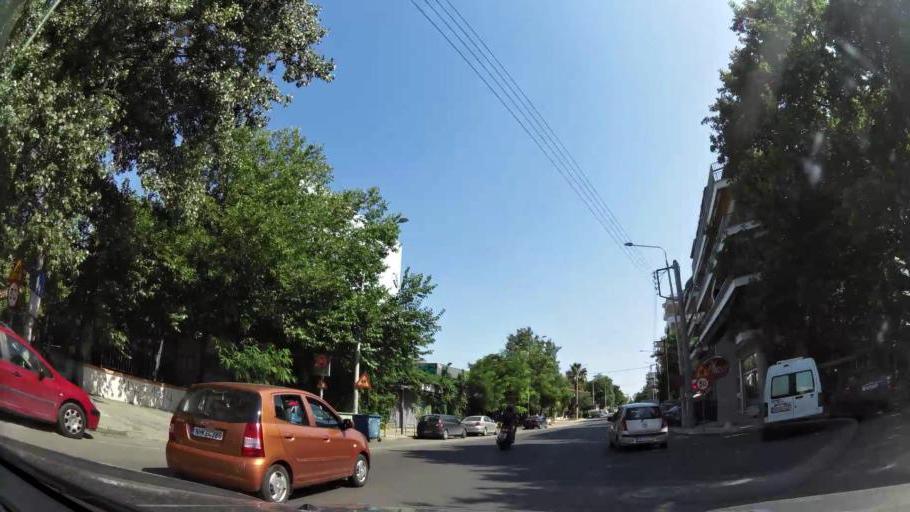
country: GR
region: Central Macedonia
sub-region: Nomos Thessalonikis
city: Kalamaria
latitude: 40.5953
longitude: 22.9536
